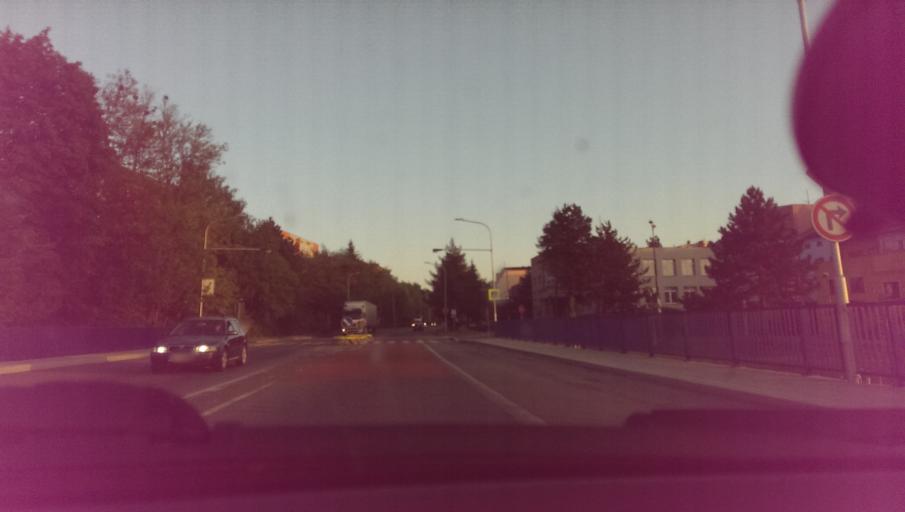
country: CZ
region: Zlin
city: Valasske Mezirici
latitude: 49.4733
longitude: 17.9726
